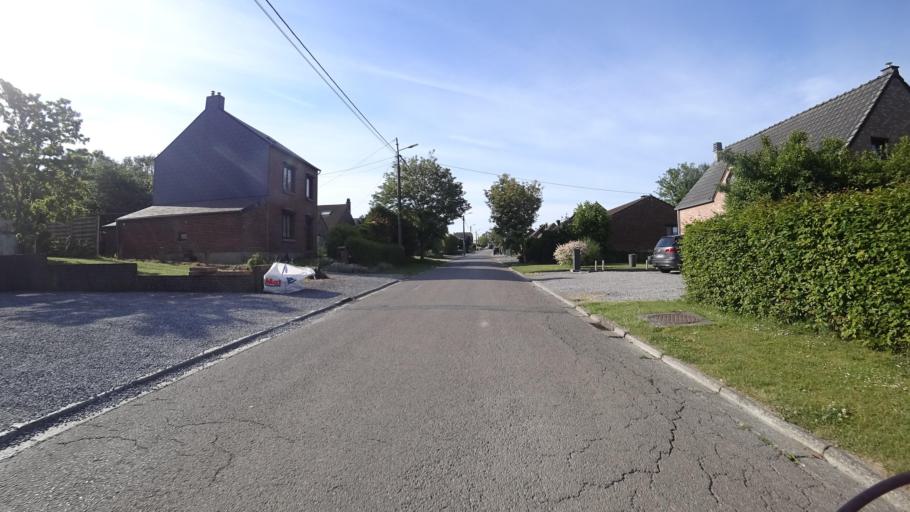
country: BE
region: Wallonia
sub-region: Province de Namur
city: Gembloux
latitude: 50.5294
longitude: 4.7534
